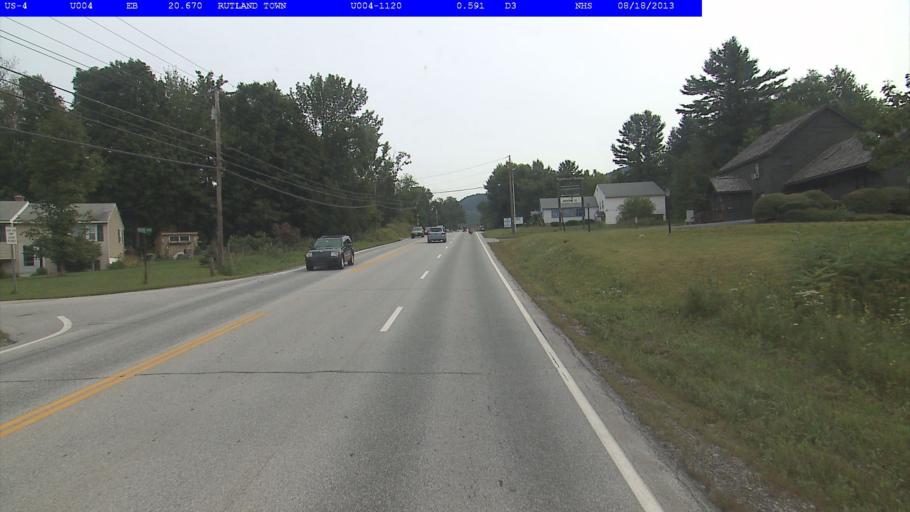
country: US
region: Vermont
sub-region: Rutland County
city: Rutland
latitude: 43.6284
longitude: -72.9466
